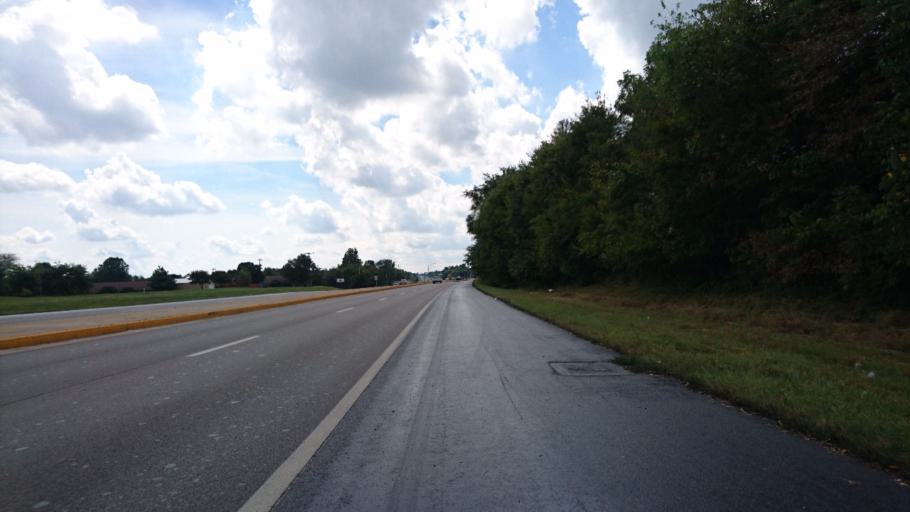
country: US
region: Missouri
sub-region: Greene County
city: Springfield
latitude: 37.2082
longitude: -93.3491
